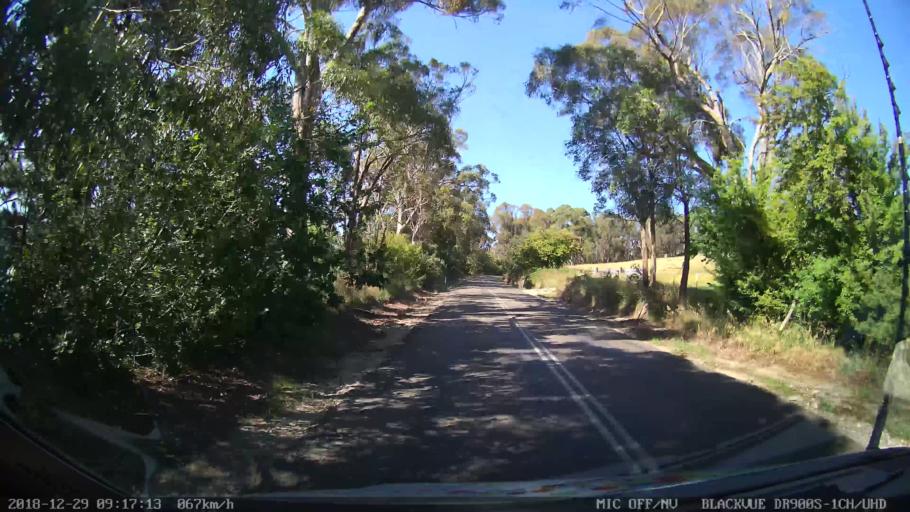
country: AU
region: New South Wales
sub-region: Upper Lachlan Shire
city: Crookwell
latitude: -34.4647
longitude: 149.4465
